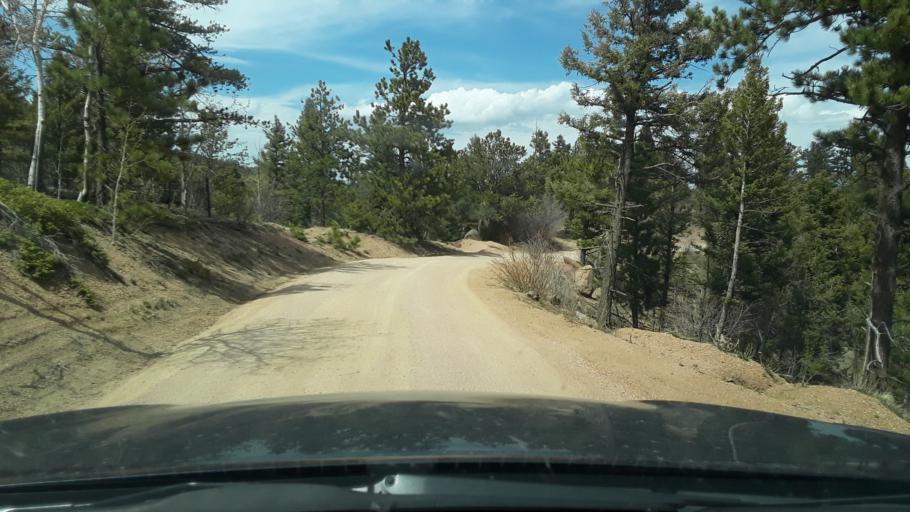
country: US
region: Colorado
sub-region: El Paso County
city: Palmer Lake
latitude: 39.0687
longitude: -104.9452
